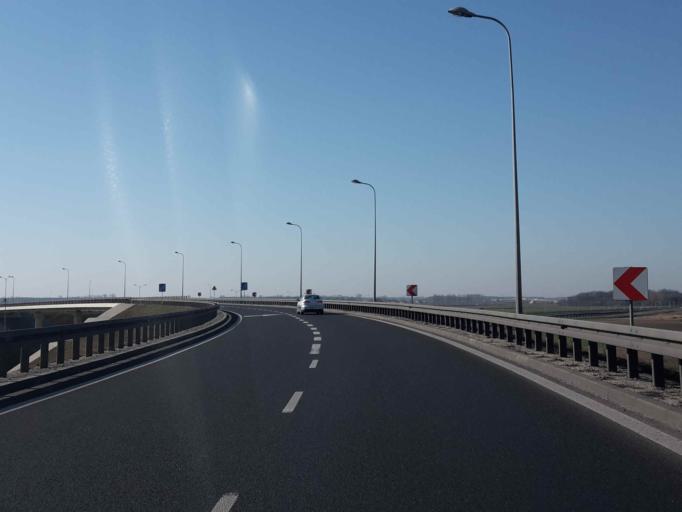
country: PL
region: Greater Poland Voivodeship
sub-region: Powiat gnieznienski
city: Lubowo
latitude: 52.5222
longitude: 17.5037
